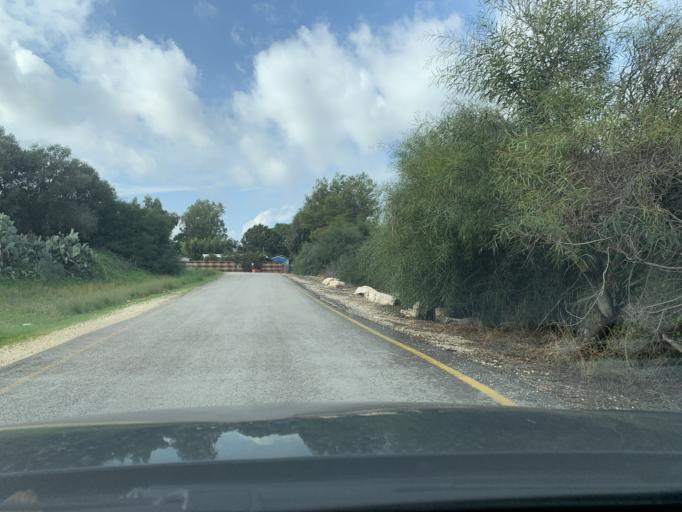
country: PS
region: West Bank
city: Qalqilyah
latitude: 32.1975
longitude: 34.9524
